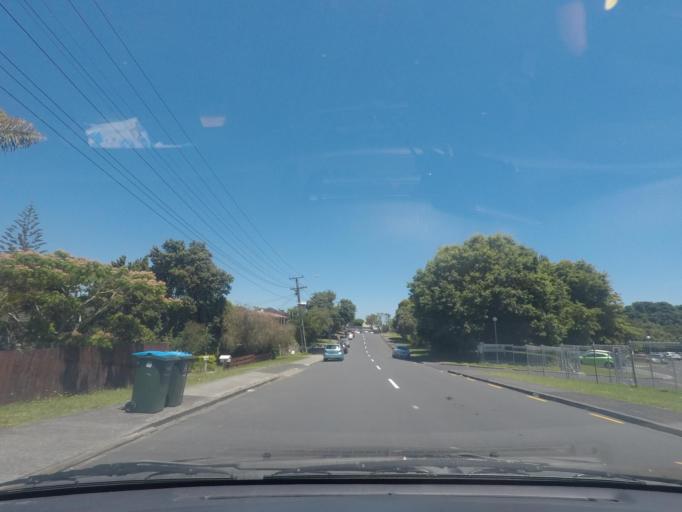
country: NZ
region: Auckland
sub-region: Auckland
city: Waitakere
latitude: -36.9206
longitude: 174.7136
